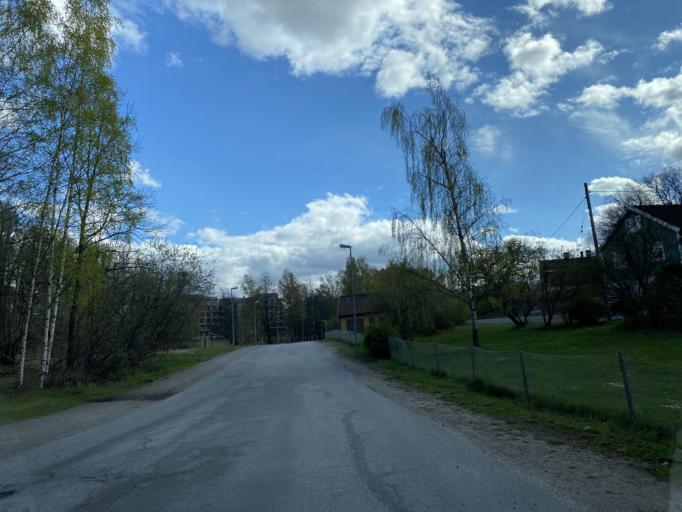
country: SE
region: Stockholm
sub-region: Stockholms Kommun
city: OEstermalm
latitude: 59.3605
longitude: 18.0857
